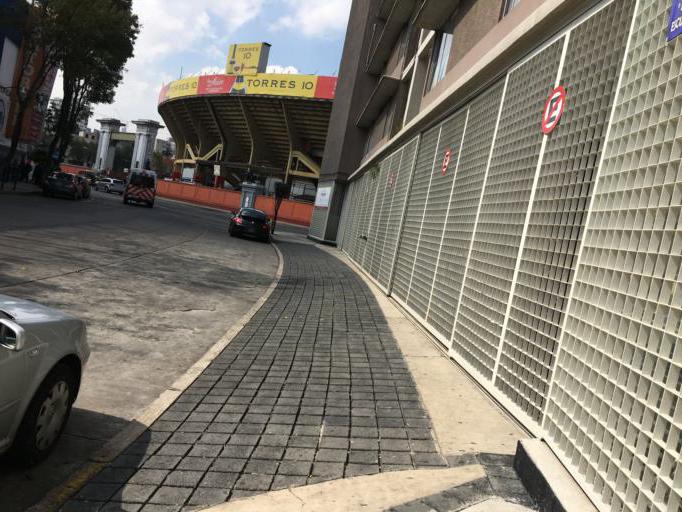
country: MX
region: Mexico City
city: Colonia del Valle
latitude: 19.3841
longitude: -99.1791
